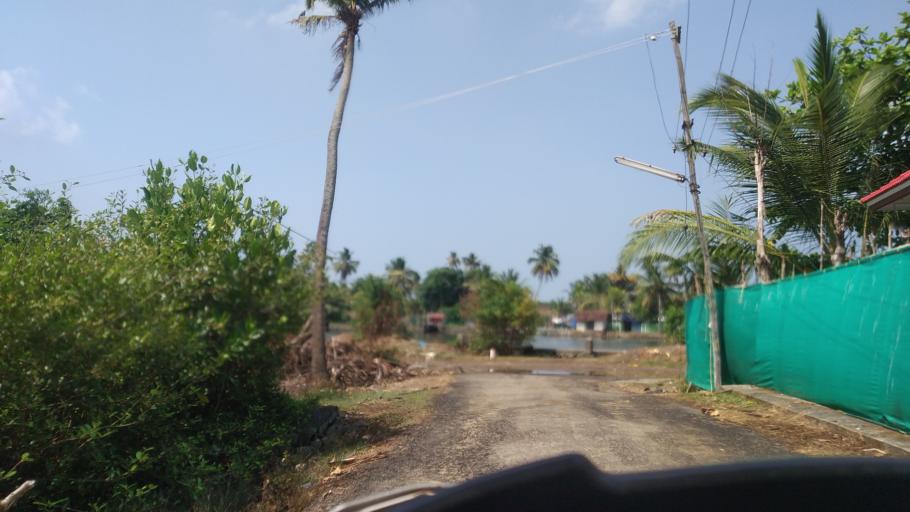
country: IN
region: Kerala
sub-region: Thrissur District
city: Kodungallur
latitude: 10.1341
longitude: 76.2070
